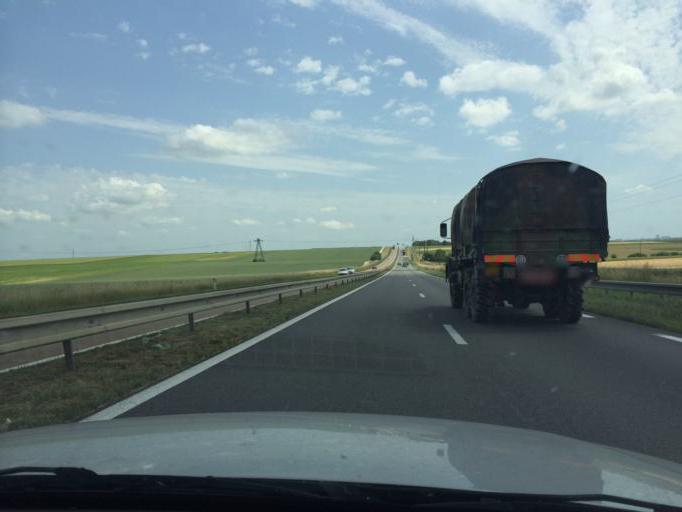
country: FR
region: Champagne-Ardenne
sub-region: Departement de la Marne
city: Fagnieres
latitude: 49.0047
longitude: 4.3348
